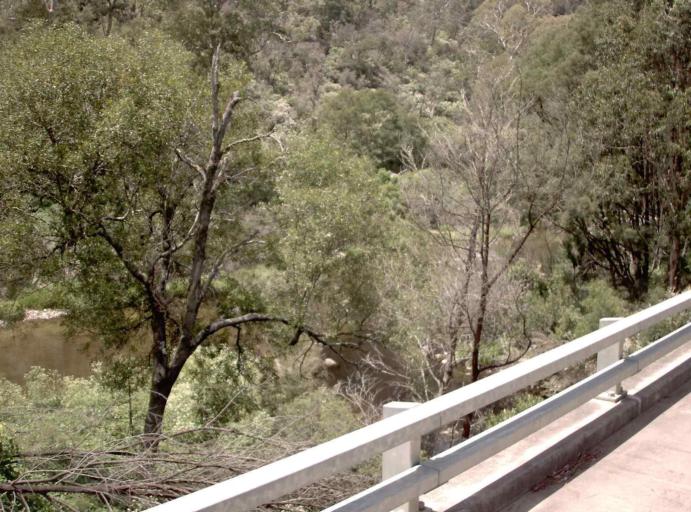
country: AU
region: Victoria
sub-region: East Gippsland
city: Lakes Entrance
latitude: -37.5399
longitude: 147.8650
